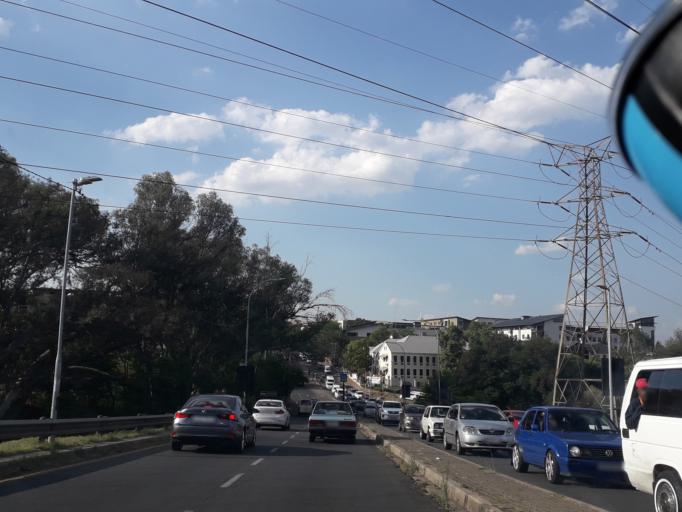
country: ZA
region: Gauteng
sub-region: City of Johannesburg Metropolitan Municipality
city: Johannesburg
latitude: -26.1384
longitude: 28.0670
